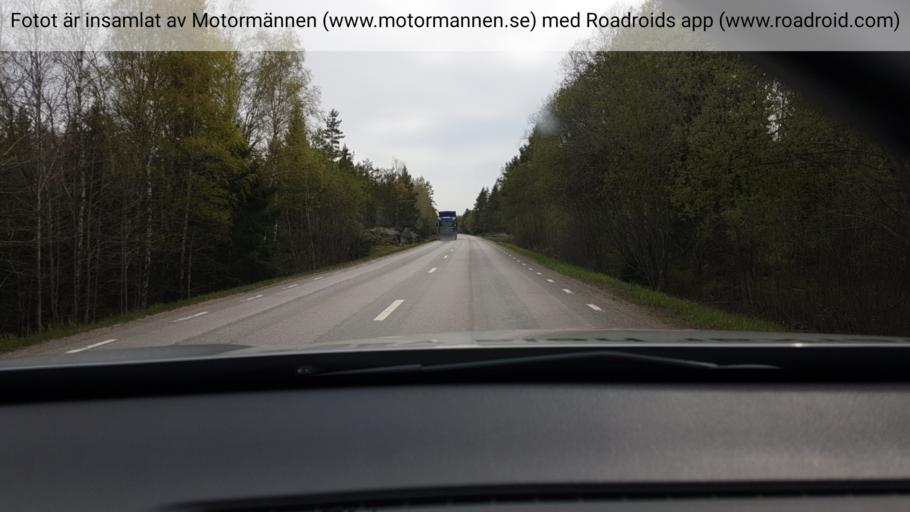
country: SE
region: Stockholm
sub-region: Norrtalje Kommun
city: Nykvarn
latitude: 59.8971
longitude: 18.0886
